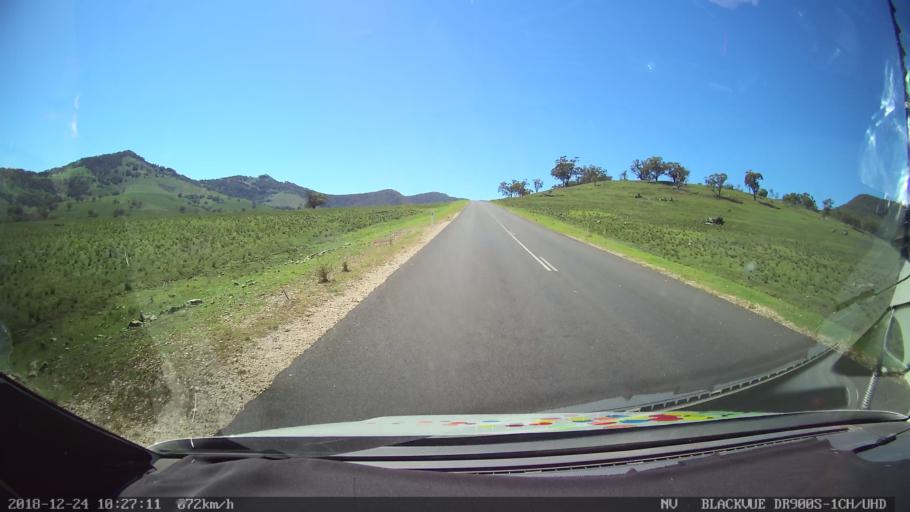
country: AU
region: New South Wales
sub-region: Liverpool Plains
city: Quirindi
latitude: -31.8149
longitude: 150.5307
